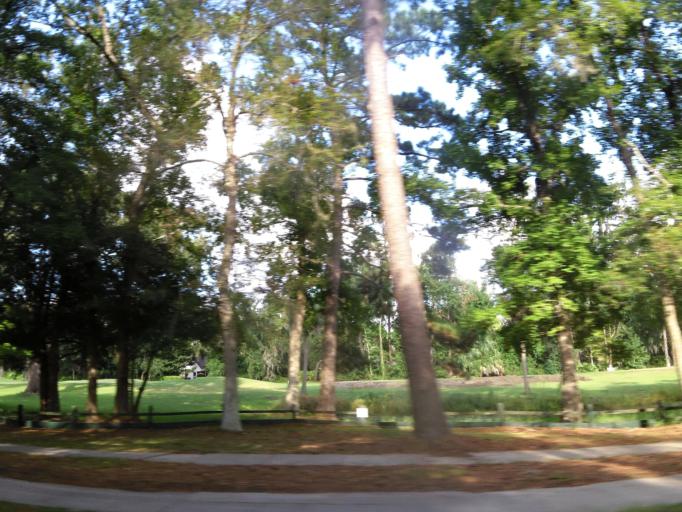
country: US
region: Georgia
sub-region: Glynn County
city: Saint Simon Mills
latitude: 31.1996
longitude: -81.3761
